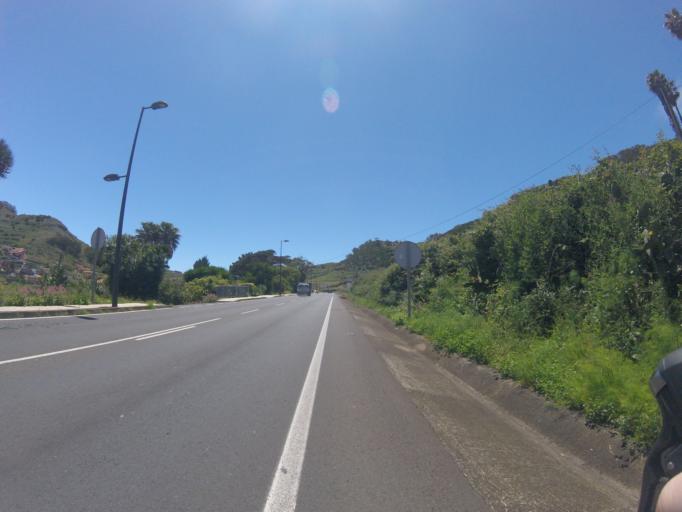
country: ES
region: Canary Islands
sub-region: Provincia de Santa Cruz de Tenerife
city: Tegueste
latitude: 28.5148
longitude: -16.3156
